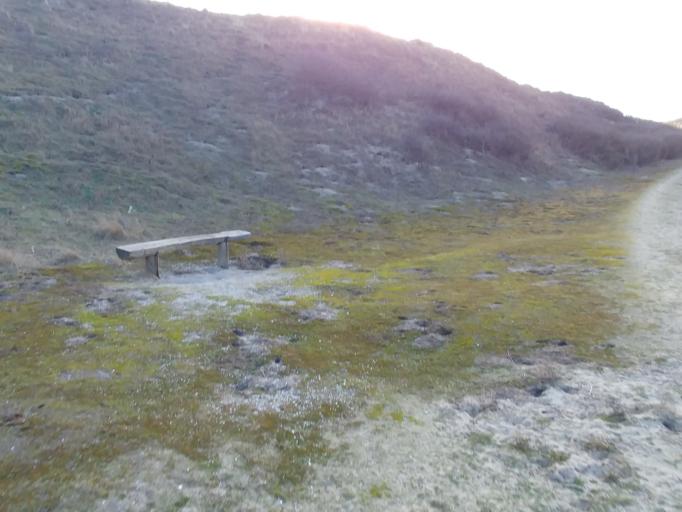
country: NL
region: South Holland
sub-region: Gemeente Den Haag
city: Scheveningen
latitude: 52.1295
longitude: 4.3083
